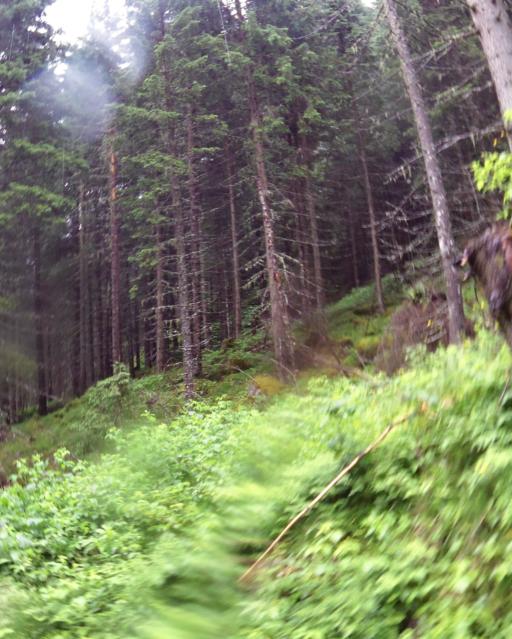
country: AT
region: Tyrol
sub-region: Politischer Bezirk Innsbruck Land
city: Neustift im Stubaital
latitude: 47.0241
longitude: 11.2212
